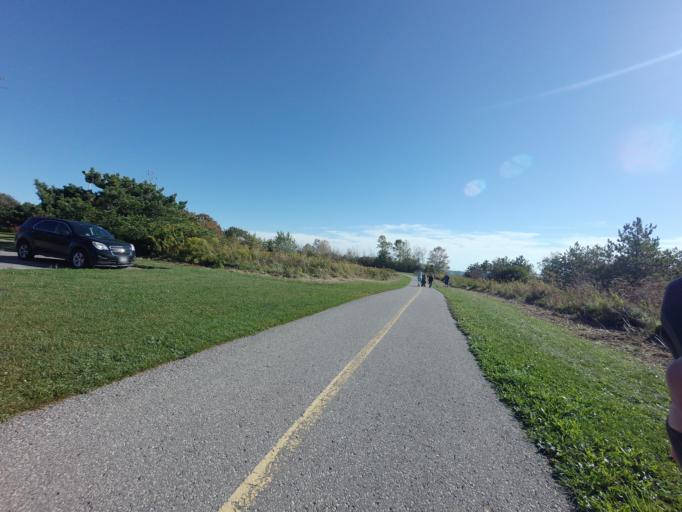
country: CA
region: Ontario
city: Oshawa
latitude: 43.8537
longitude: -78.8818
